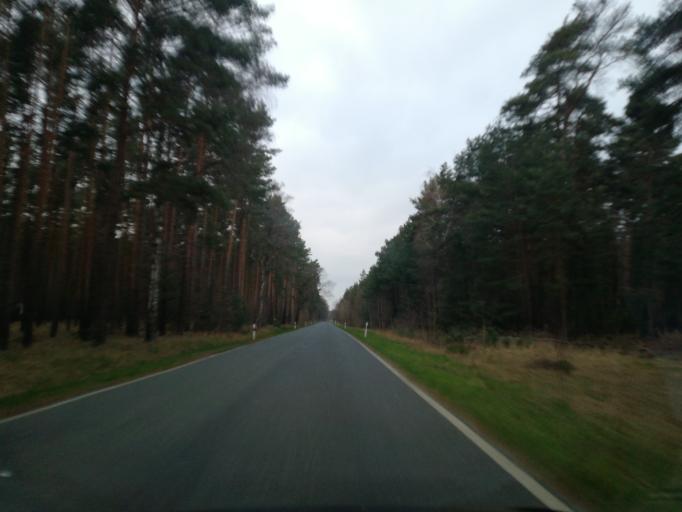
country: DE
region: Brandenburg
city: Vetschau
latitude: 51.7610
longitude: 14.0887
